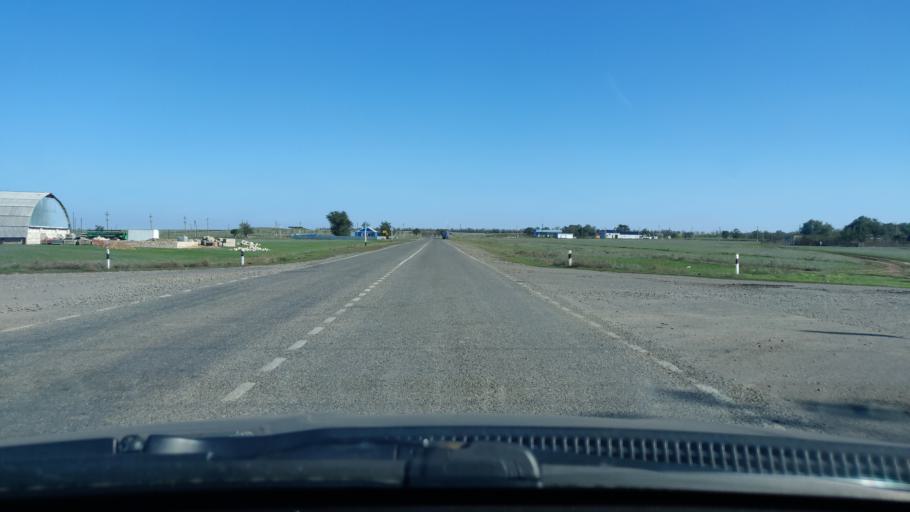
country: RU
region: Stavropol'skiy
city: Letnyaya Stavka
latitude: 45.3745
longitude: 43.6864
